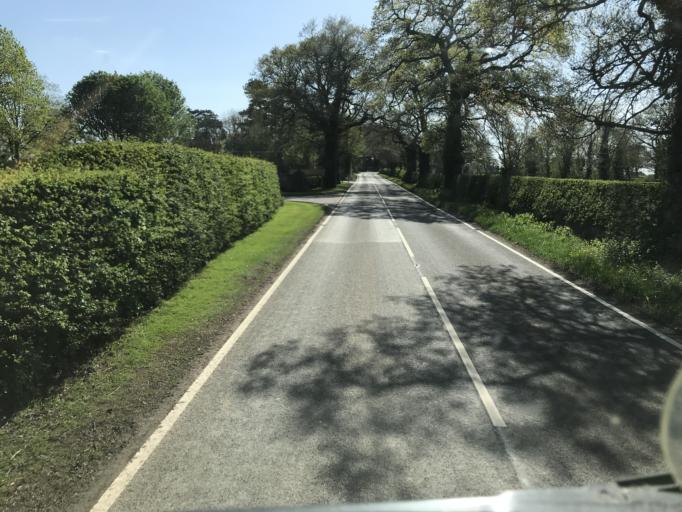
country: GB
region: England
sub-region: Cheshire East
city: Nantwich
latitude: 53.0967
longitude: -2.5130
